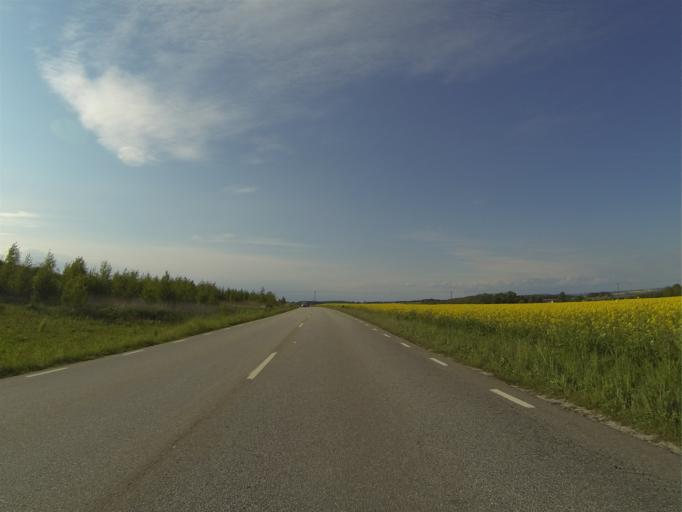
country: SE
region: Skane
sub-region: Lunds Kommun
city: Lund
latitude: 55.7042
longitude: 13.3031
